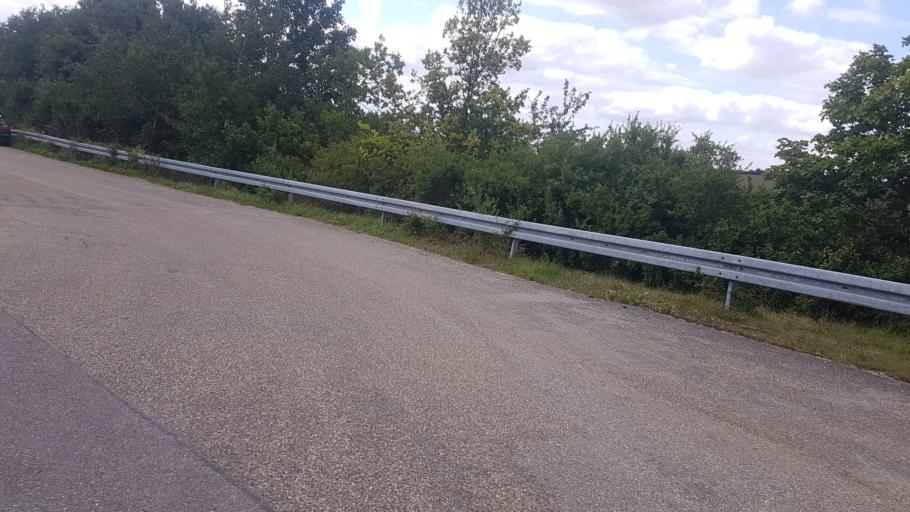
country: DE
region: Bavaria
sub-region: Regierungsbezirk Mittelfranken
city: Neusitz
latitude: 49.3751
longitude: 10.2266
